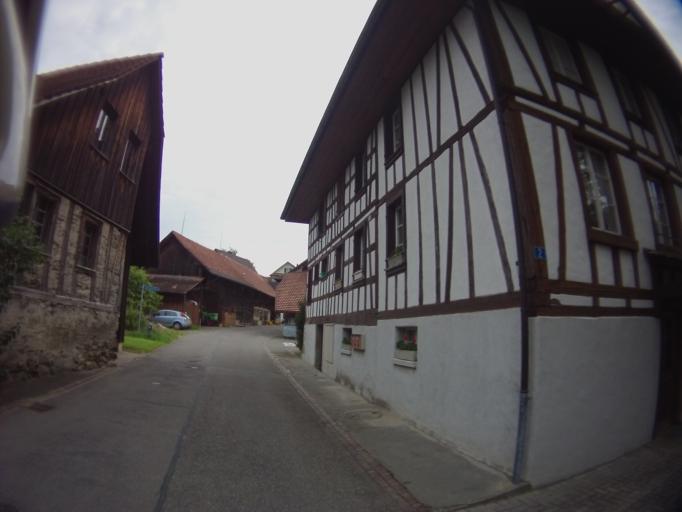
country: CH
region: Zurich
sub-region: Bezirk Affoltern
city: Knonau
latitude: 47.2261
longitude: 8.4845
